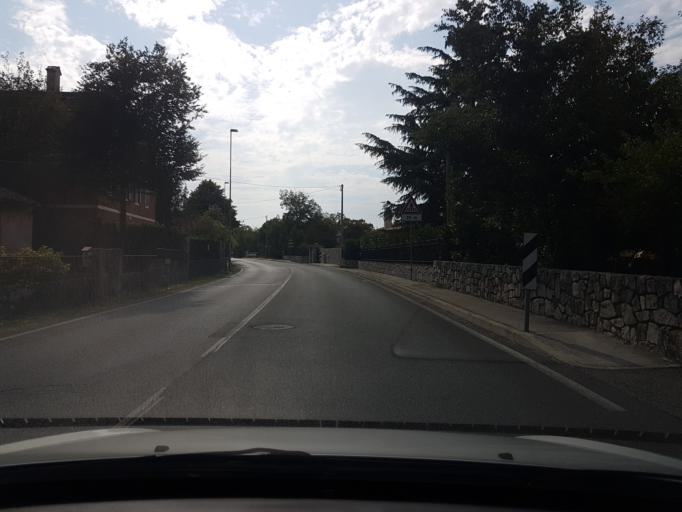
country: IT
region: Friuli Venezia Giulia
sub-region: Provincia di Trieste
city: Aurisina Cave
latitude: 45.7544
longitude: 13.6653
